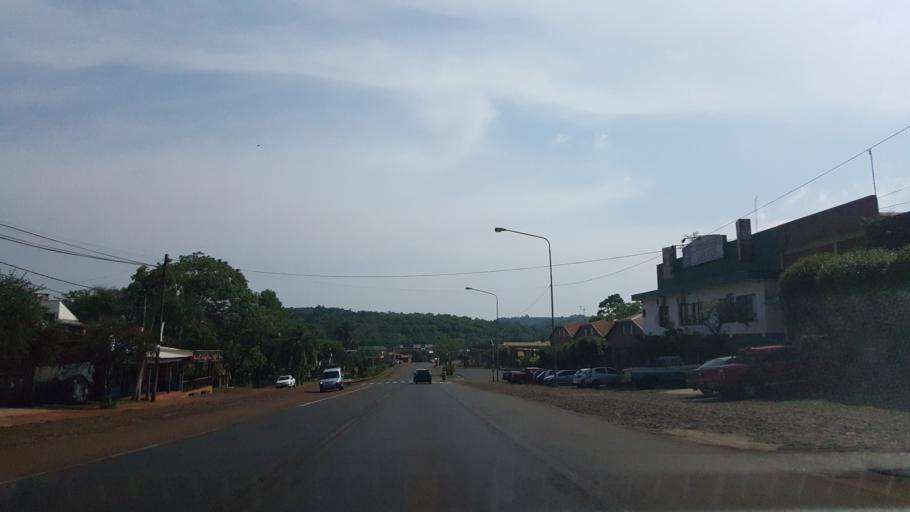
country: AR
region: Misiones
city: Capiovi
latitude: -26.9280
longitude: -55.0602
